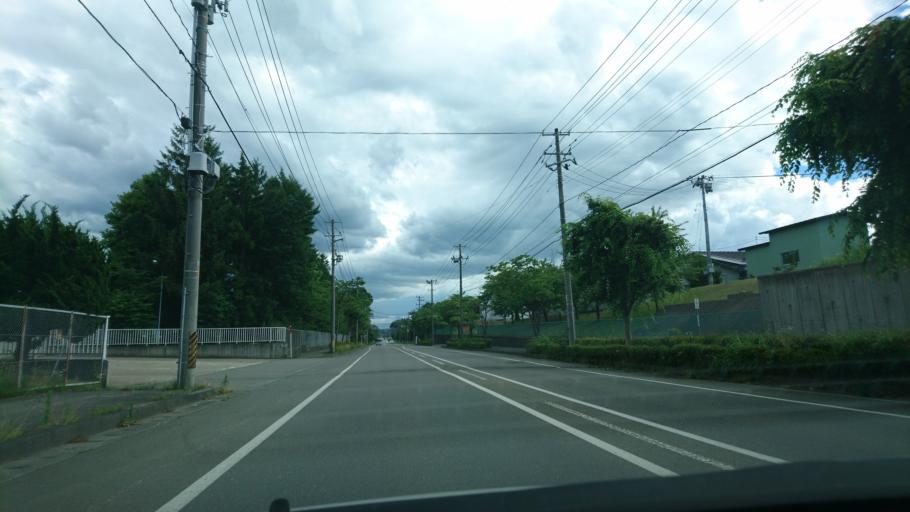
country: JP
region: Iwate
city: Kitakami
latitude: 39.3310
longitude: 141.1280
